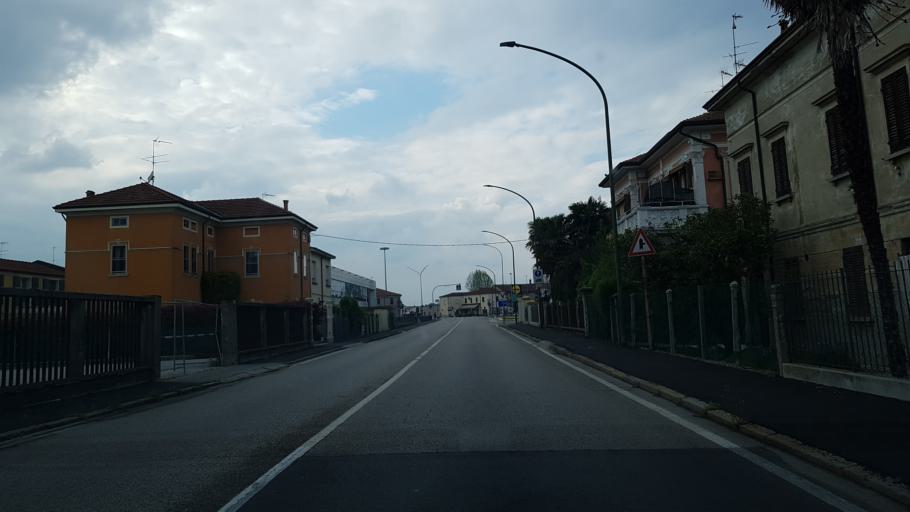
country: IT
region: Lombardy
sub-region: Provincia di Mantova
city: Ostiglia
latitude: 45.0703
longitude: 11.1365
